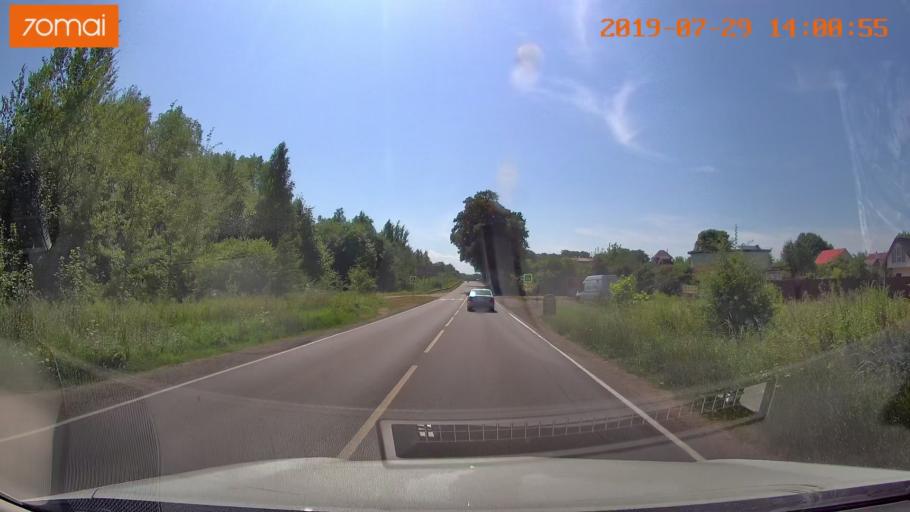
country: RU
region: Kaliningrad
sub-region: Gorod Kaliningrad
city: Baltiysk
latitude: 54.6747
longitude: 19.9252
